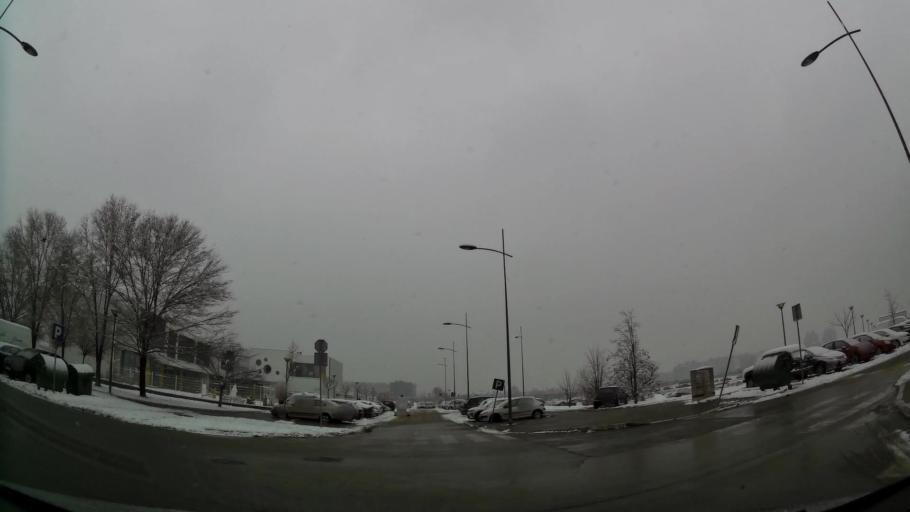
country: RS
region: Central Serbia
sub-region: Belgrade
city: Novi Beograd
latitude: 44.8054
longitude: 20.4108
